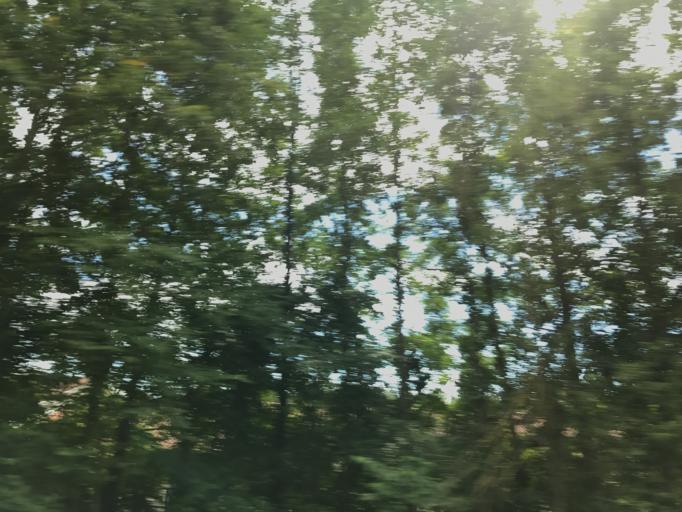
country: DE
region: Baden-Wuerttemberg
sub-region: Tuebingen Region
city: Wangen im Allgau
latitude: 47.7068
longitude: 9.8136
